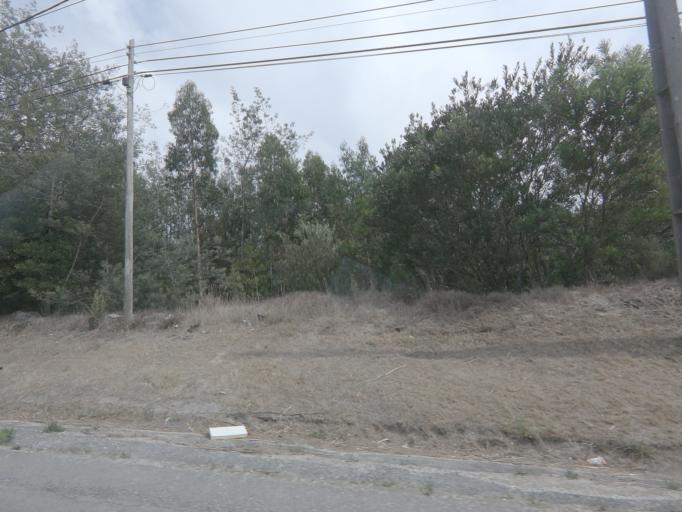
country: PT
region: Leiria
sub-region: Leiria
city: Caranguejeira
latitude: 39.8164
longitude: -8.7305
